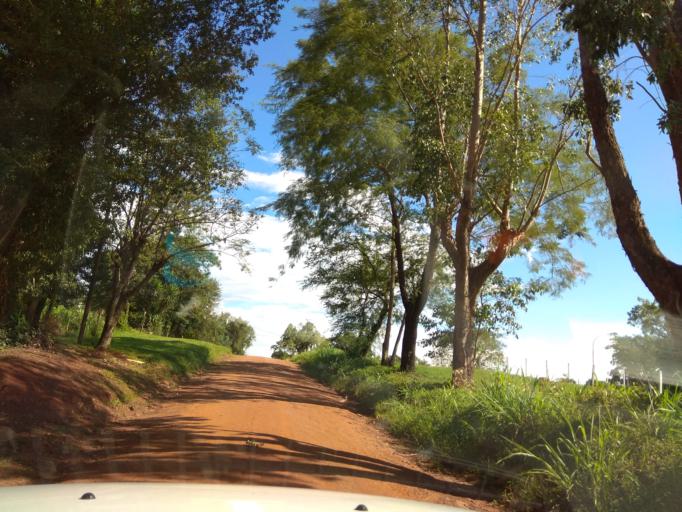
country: AR
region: Misiones
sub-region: Departamento de Candelaria
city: Candelaria
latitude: -27.4536
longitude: -55.7542
